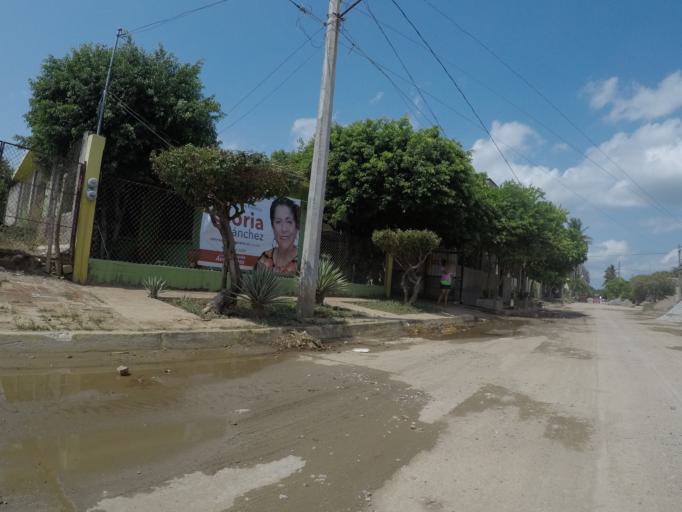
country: MX
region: Oaxaca
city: Union Hidalgo
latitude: 16.4699
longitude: -94.8289
